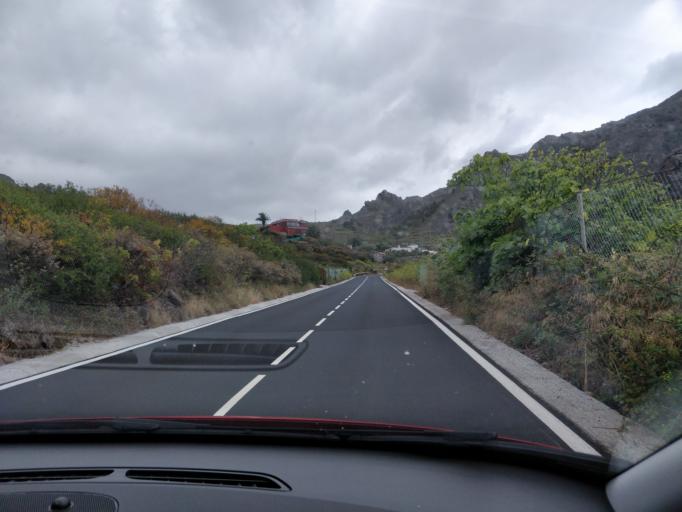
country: ES
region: Canary Islands
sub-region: Provincia de Santa Cruz de Tenerife
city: Tanque
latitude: 28.3540
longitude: -16.8441
